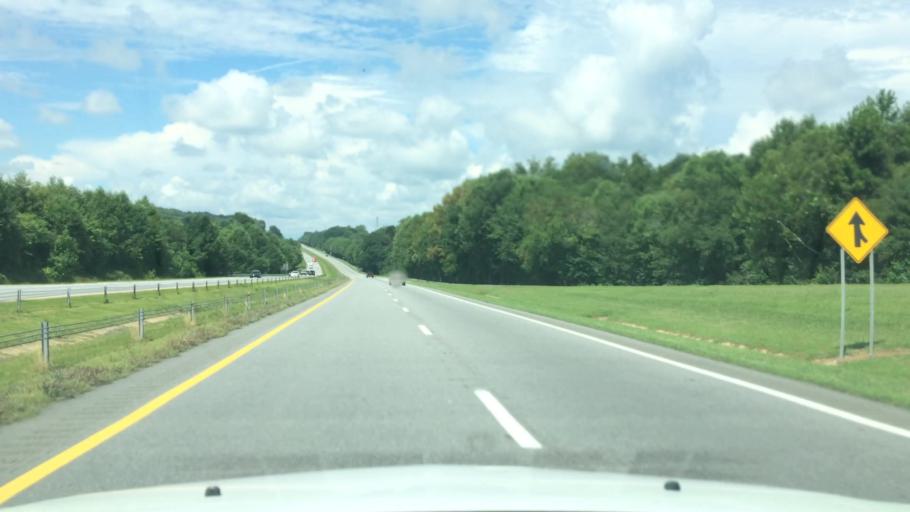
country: US
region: North Carolina
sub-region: Wilkes County
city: North Wilkesboro
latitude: 36.1504
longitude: -81.0198
